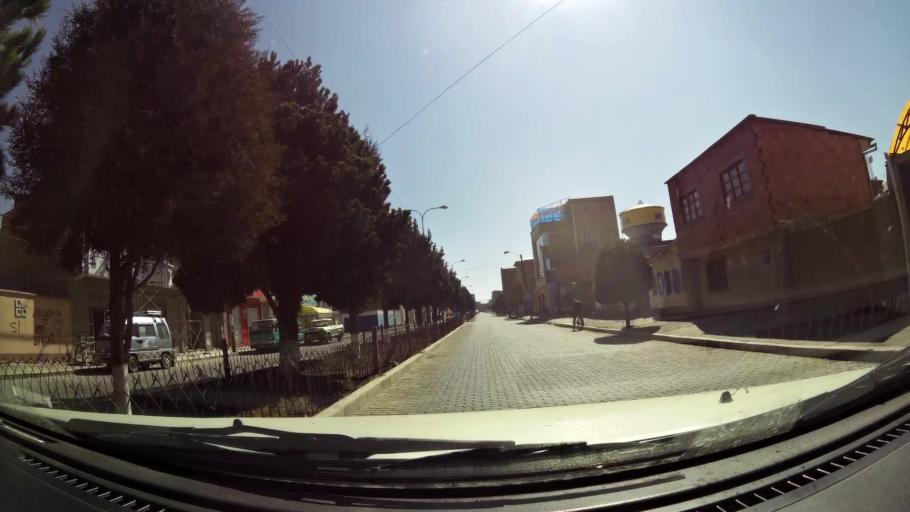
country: BO
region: La Paz
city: La Paz
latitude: -16.5204
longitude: -68.1522
